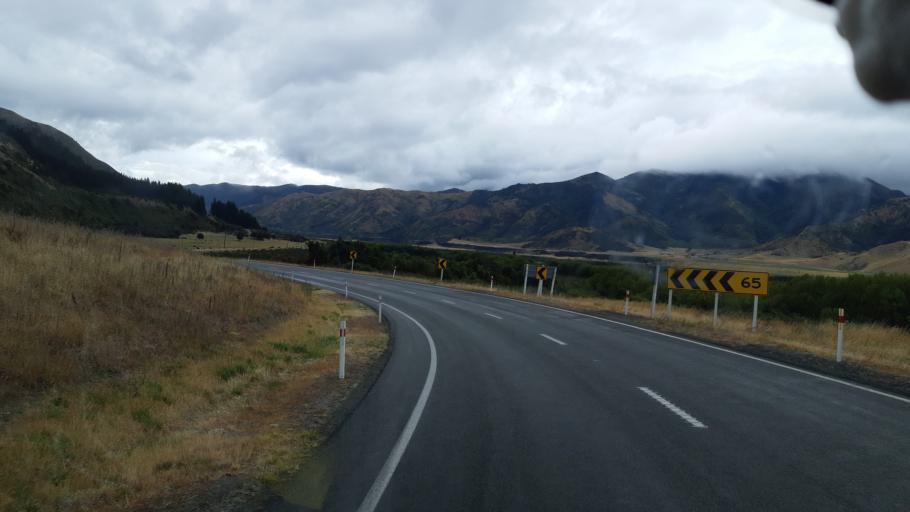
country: NZ
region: Canterbury
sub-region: Hurunui District
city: Amberley
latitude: -42.5713
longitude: 172.7098
